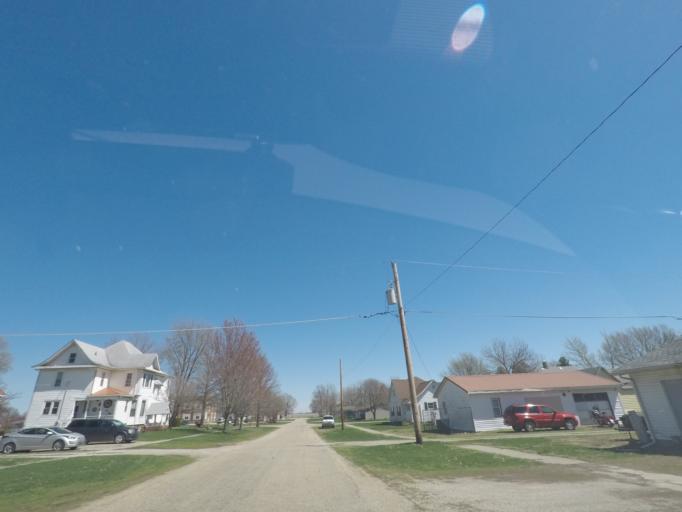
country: US
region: Illinois
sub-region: Macon County
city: Warrensburg
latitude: 39.9664
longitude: -89.1598
